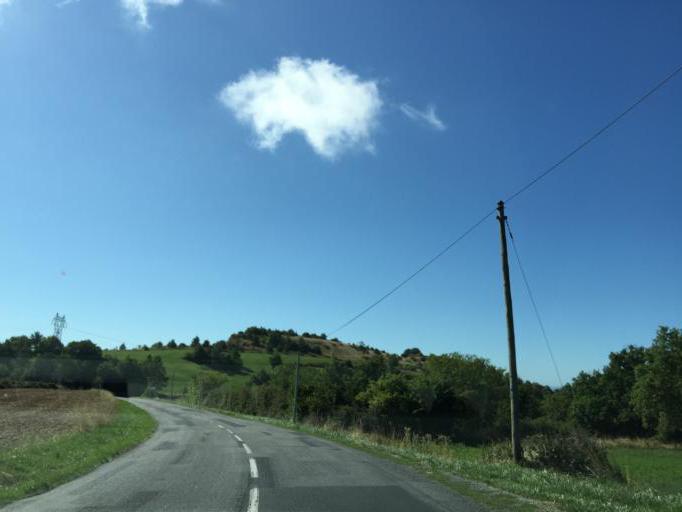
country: FR
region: Midi-Pyrenees
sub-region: Departement de l'Aveyron
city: Saint-Georges-de-Luzencon
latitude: 44.1106
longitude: 2.9032
